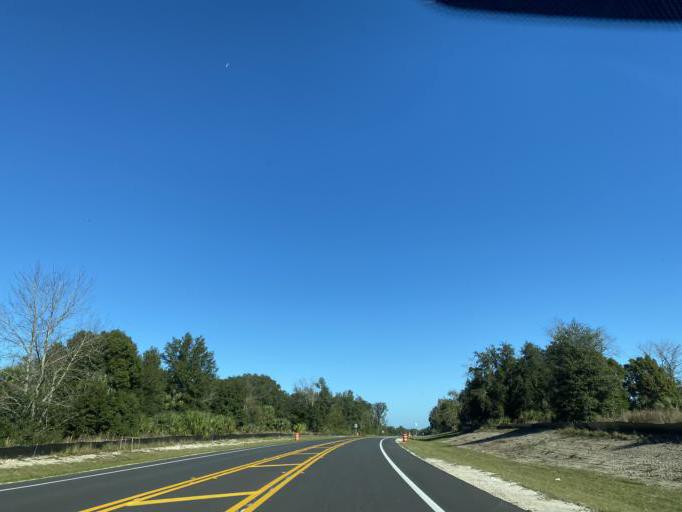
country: US
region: Florida
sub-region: Lake County
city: Mount Plymouth
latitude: 28.8182
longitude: -81.5223
